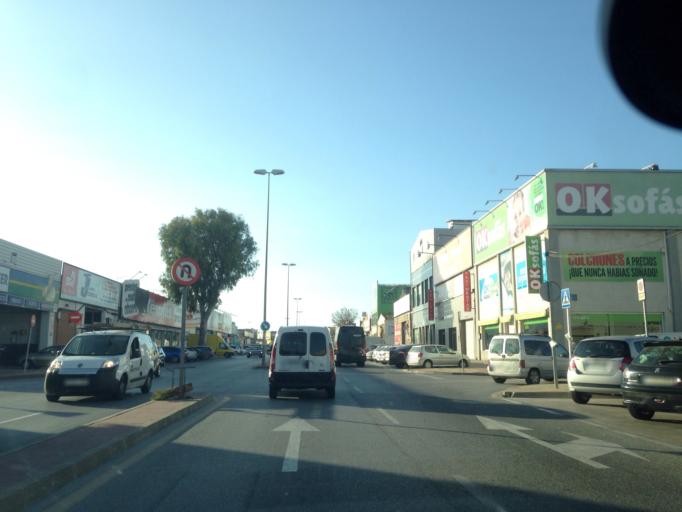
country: ES
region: Andalusia
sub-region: Provincia de Malaga
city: Malaga
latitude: 36.7127
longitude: -4.4830
